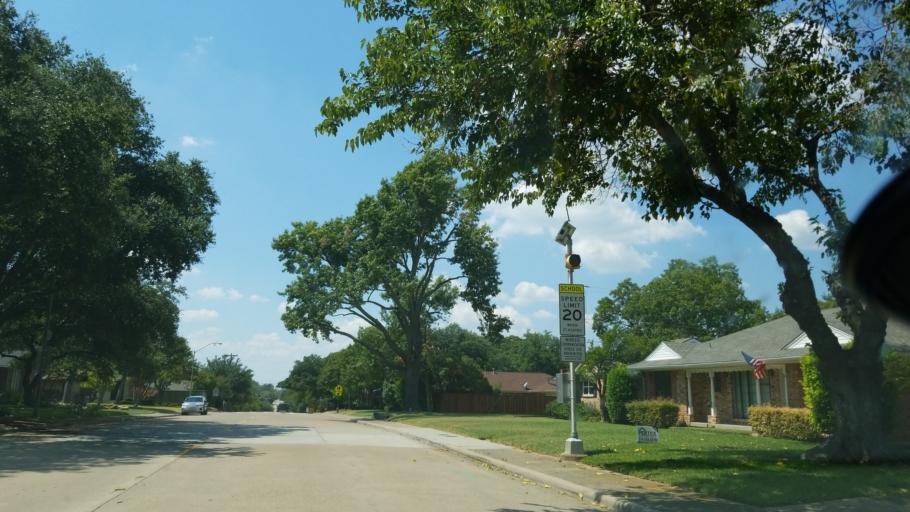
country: US
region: Texas
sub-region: Dallas County
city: Richardson
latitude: 32.8862
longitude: -96.7060
